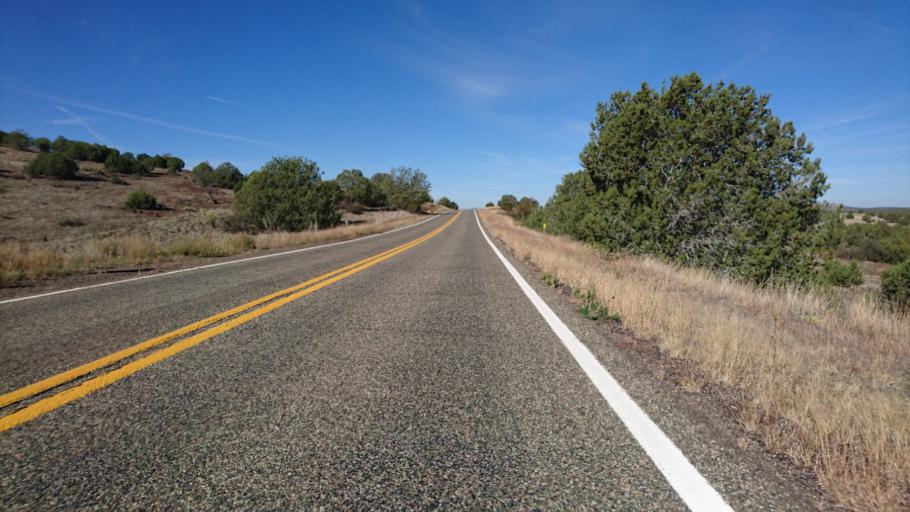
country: US
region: Arizona
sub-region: Yavapai County
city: Paulden
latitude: 35.2810
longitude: -112.7072
